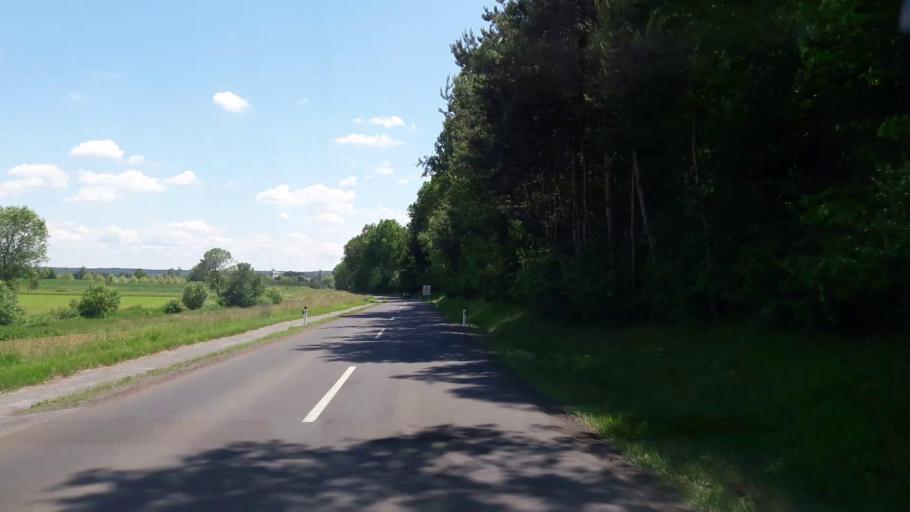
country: AT
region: Burgenland
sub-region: Politischer Bezirk Jennersdorf
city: Jennersdorf
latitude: 46.9464
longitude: 16.1256
